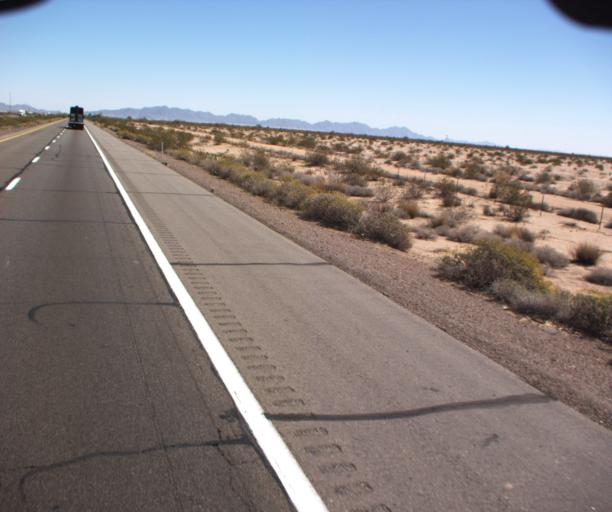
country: US
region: Arizona
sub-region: Yuma County
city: Wellton
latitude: 32.6887
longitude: -113.9839
